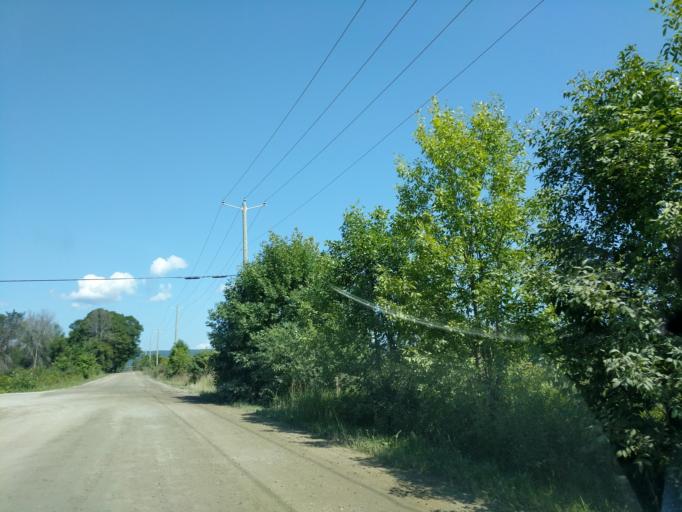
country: CA
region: Ontario
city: Bells Corners
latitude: 45.4472
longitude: -75.9031
